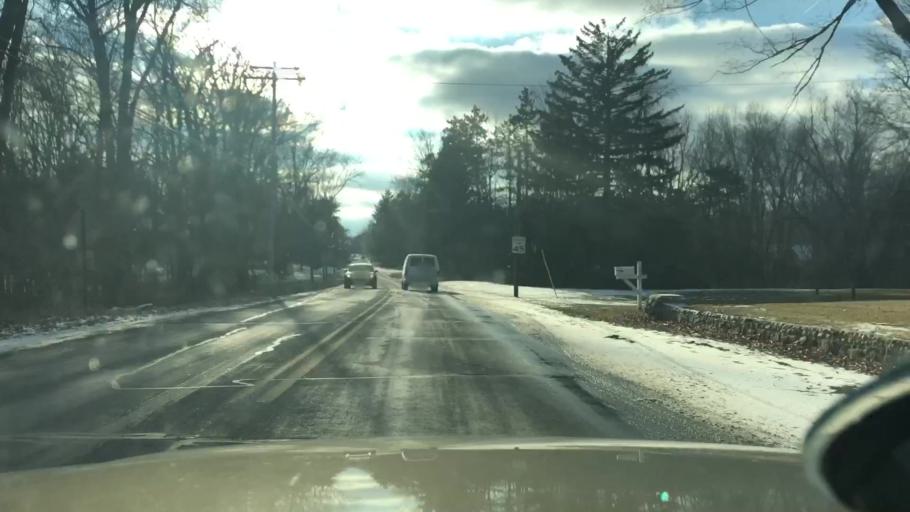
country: US
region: Michigan
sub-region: Jackson County
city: Vandercook Lake
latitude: 42.1983
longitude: -84.4426
